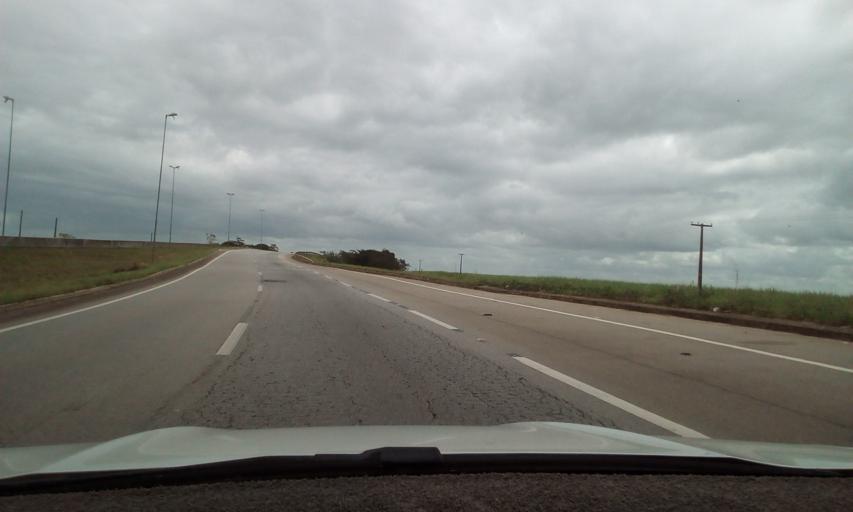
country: BR
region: Paraiba
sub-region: Mamanguape
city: Mamanguape
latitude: -6.9289
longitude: -35.1044
